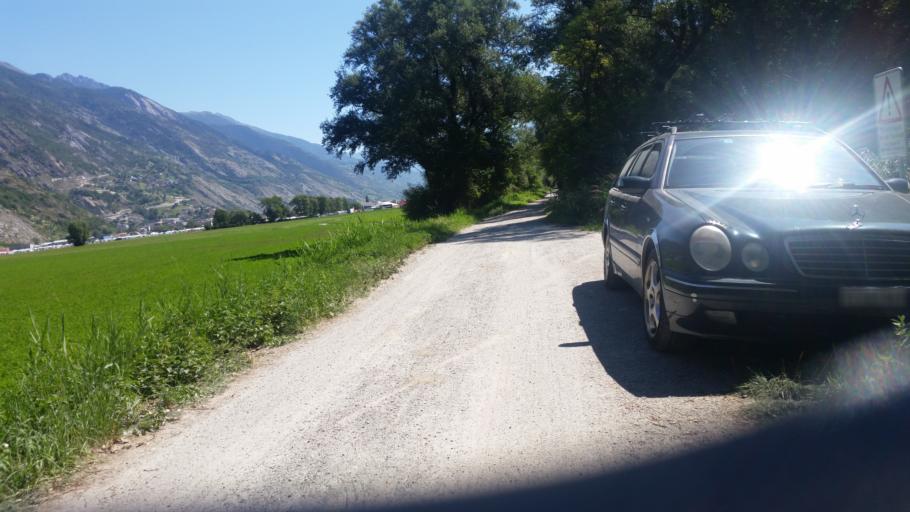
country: CH
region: Valais
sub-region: Leuk District
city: Turtmann
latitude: 46.3099
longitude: 7.7160
